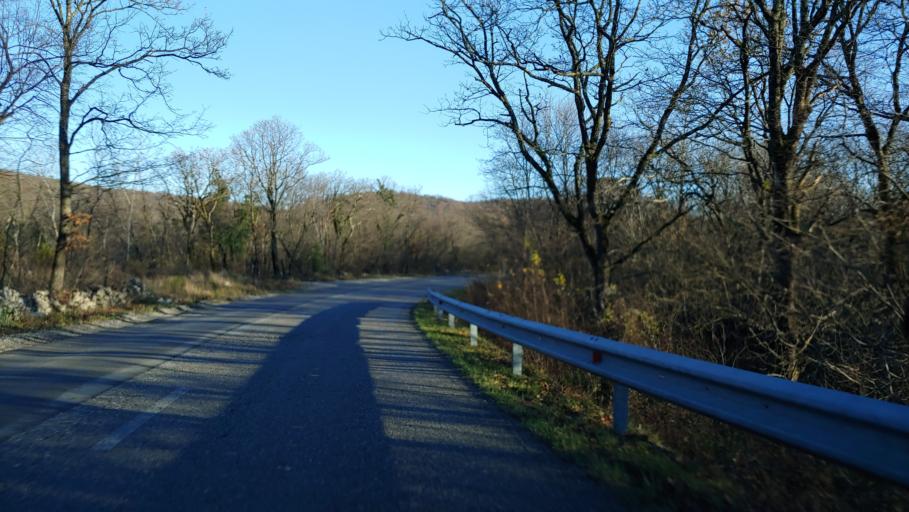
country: SI
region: Sezana
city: Sezana
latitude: 45.7050
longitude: 13.8431
